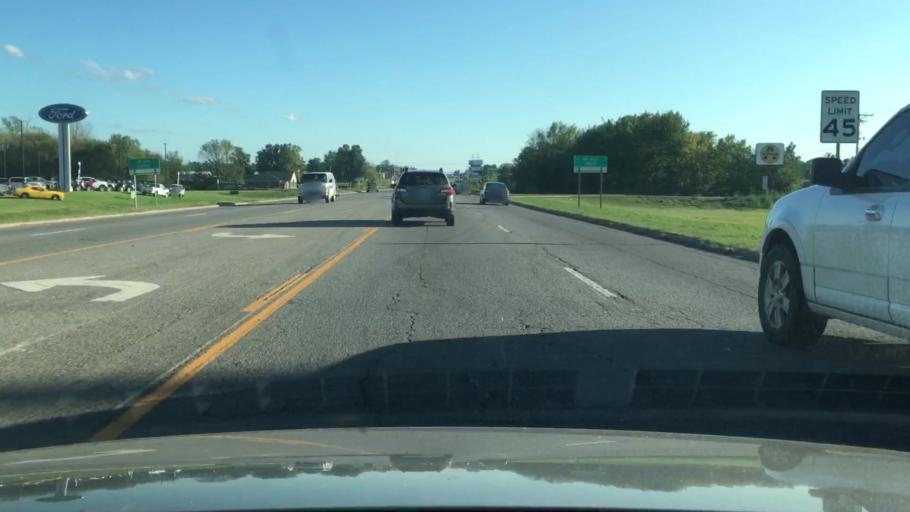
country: US
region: Oklahoma
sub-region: Cherokee County
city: Park Hill
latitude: 35.8751
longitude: -94.9763
